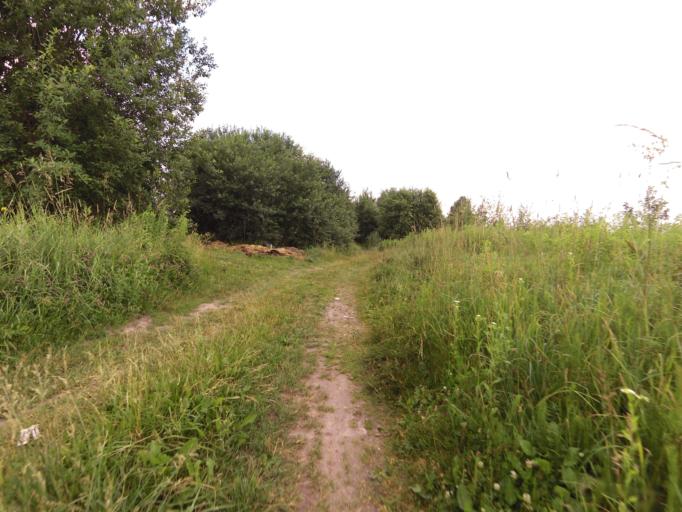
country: LT
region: Vilnius County
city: Pasilaiciai
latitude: 54.7552
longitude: 25.2197
